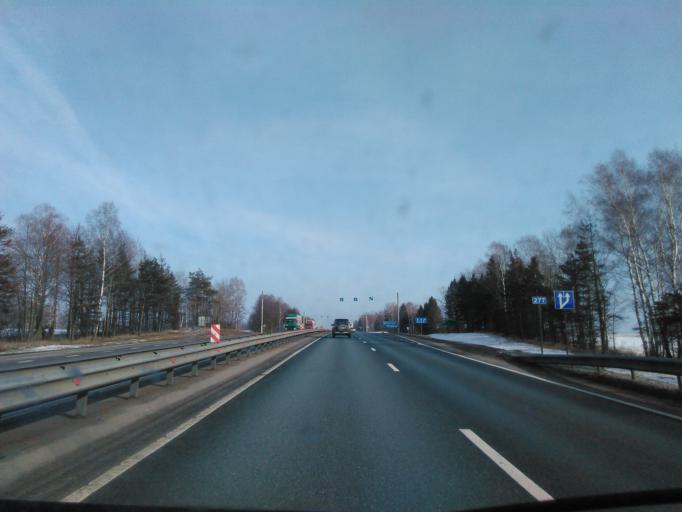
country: RU
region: Smolensk
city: Verkhnedneprovskiy
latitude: 55.1821
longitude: 33.5443
